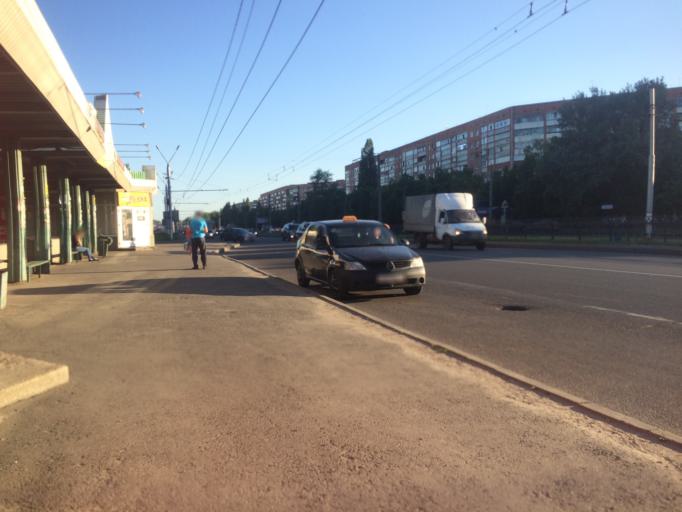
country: RU
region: Kursk
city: Kursk
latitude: 51.6717
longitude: 36.1434
